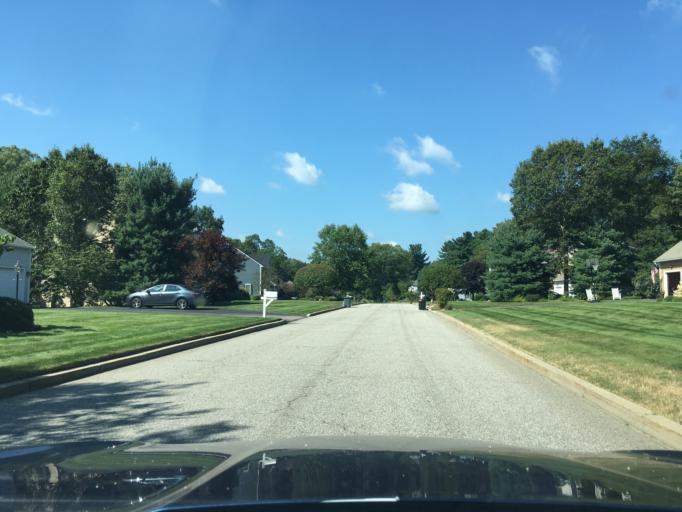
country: US
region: Rhode Island
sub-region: Kent County
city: East Greenwich
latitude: 41.6342
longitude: -71.4713
